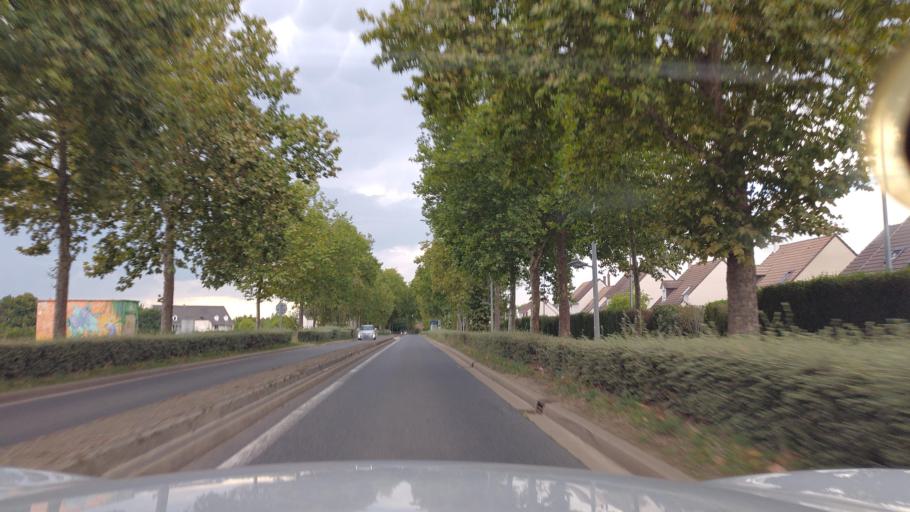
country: FR
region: Ile-de-France
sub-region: Departement de Seine-et-Marne
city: Brie-Comte-Robert
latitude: 48.6862
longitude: 2.6237
